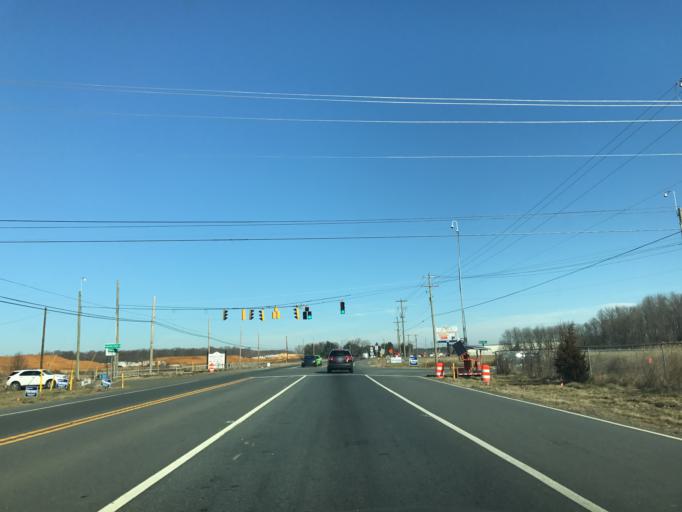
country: US
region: Delaware
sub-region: New Castle County
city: Middletown
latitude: 39.4800
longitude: -75.7202
